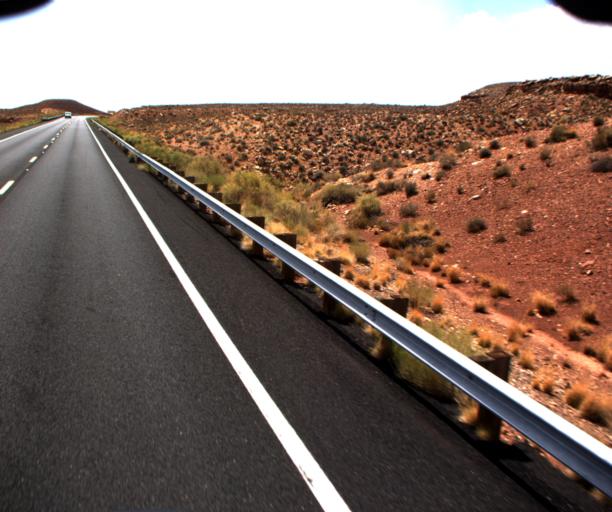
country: US
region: Arizona
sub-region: Coconino County
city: Tuba City
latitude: 35.9100
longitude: -111.5549
